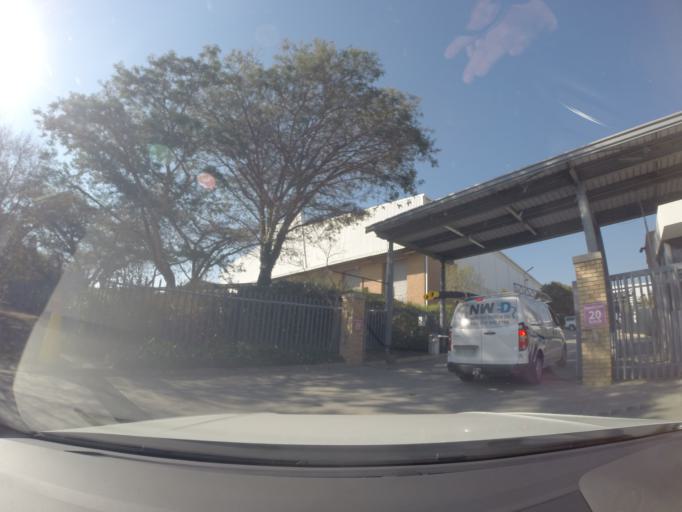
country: ZA
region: Gauteng
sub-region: City of Johannesburg Metropolitan Municipality
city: Modderfontein
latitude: -26.0979
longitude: 28.1265
